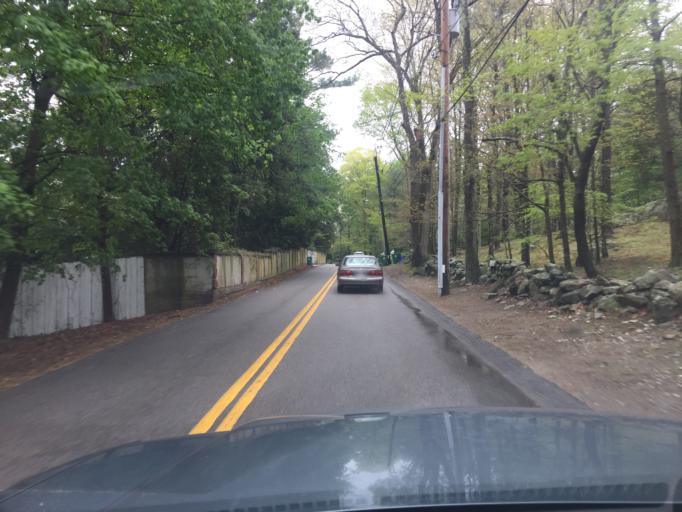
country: US
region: Massachusetts
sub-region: Norfolk County
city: Westwood
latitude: 42.2277
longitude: -71.2142
